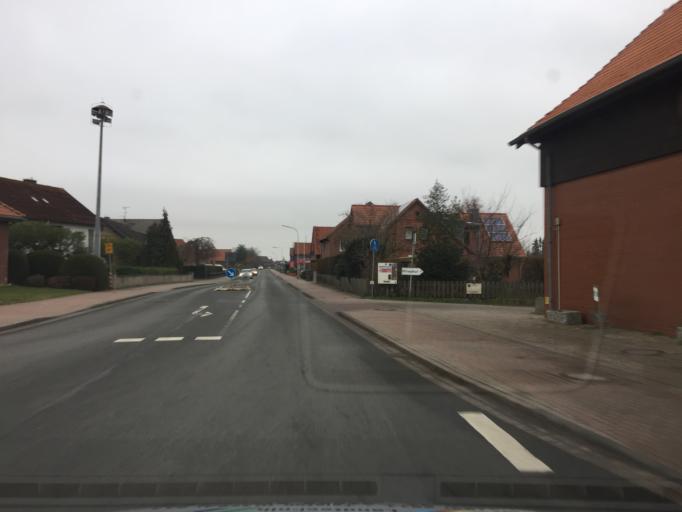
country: DE
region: Lower Saxony
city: Meerbeck
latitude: 52.3424
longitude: 9.1447
